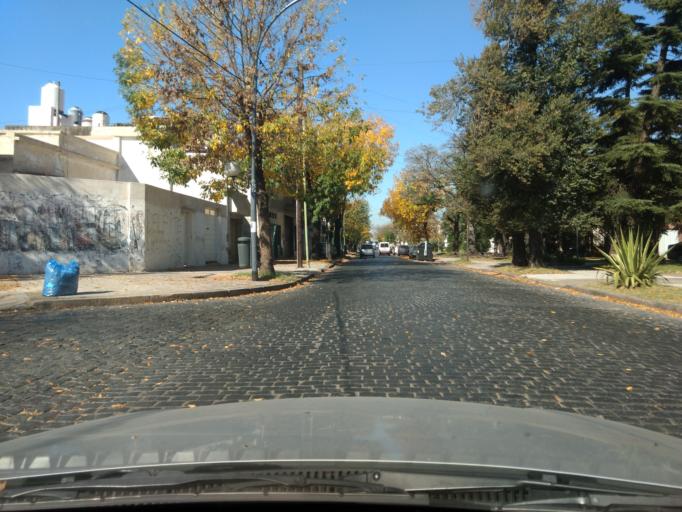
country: AR
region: Buenos Aires F.D.
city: Villa Lugano
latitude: -34.6473
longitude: -58.4724
